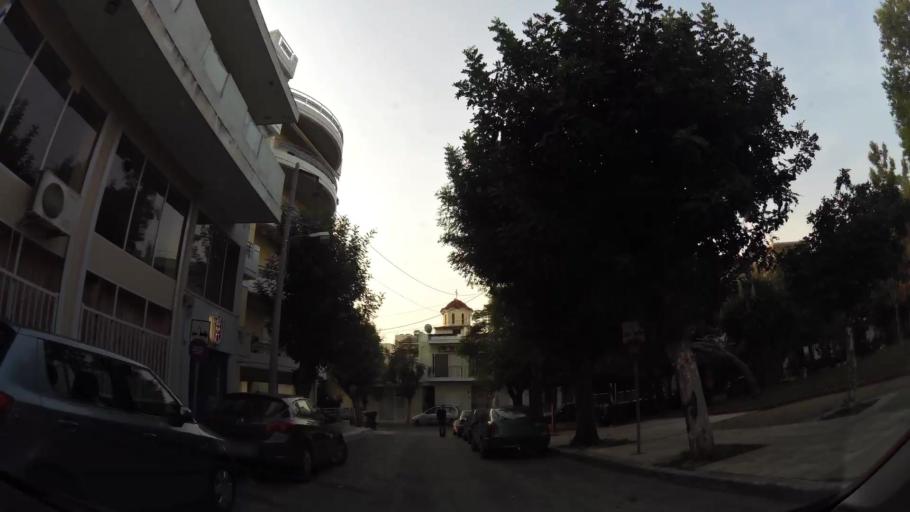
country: GR
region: Attica
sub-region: Nomarchia Athinas
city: Peristeri
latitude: 38.0219
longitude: 23.6899
